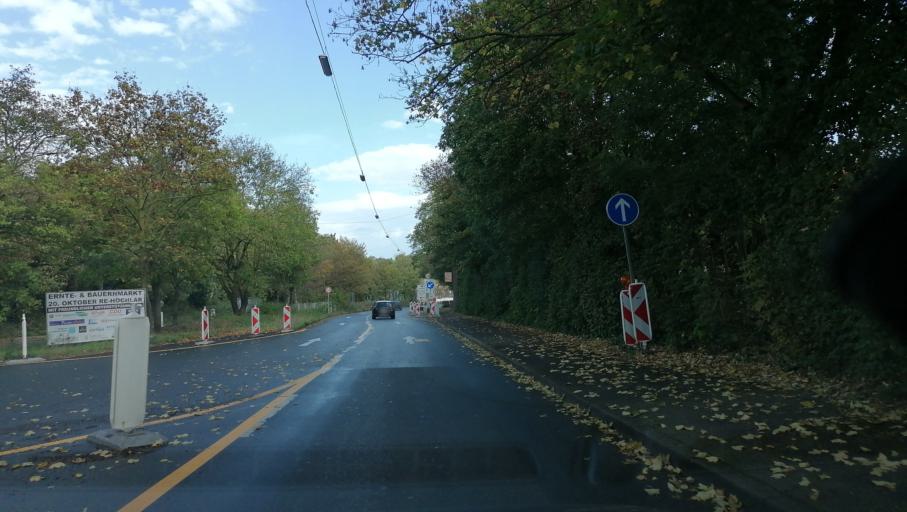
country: DE
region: North Rhine-Westphalia
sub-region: Regierungsbezirk Munster
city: Recklinghausen
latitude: 51.6070
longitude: 7.1713
